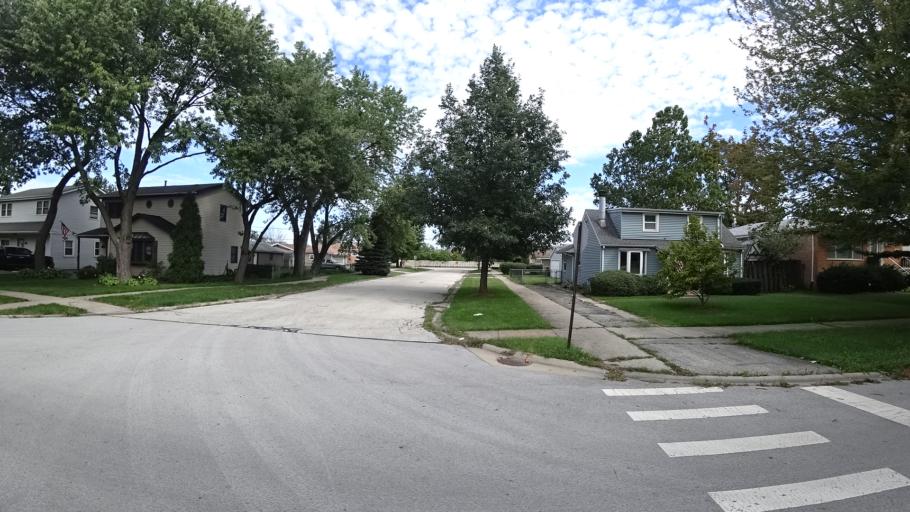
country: US
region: Illinois
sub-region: Cook County
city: Chicago Ridge
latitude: 41.7158
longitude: -87.7859
